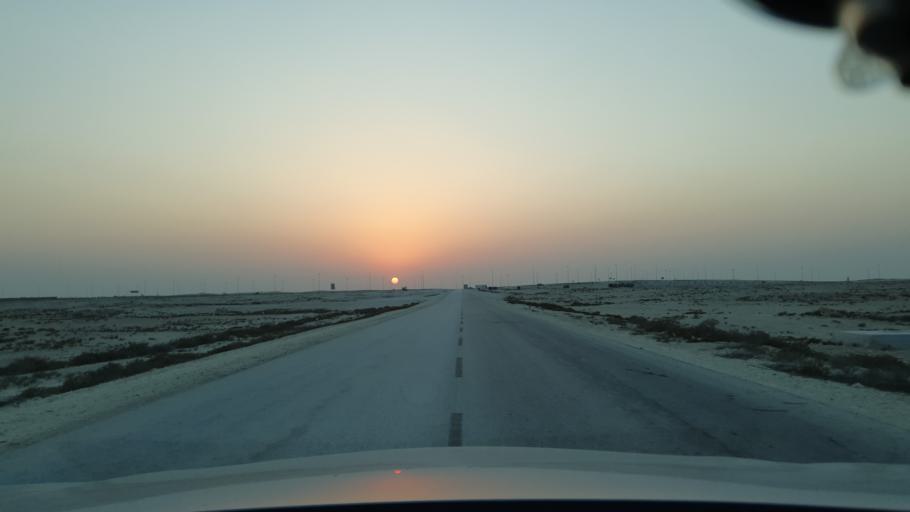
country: BH
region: Central Governorate
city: Dar Kulayb
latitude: 25.9558
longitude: 50.6012
